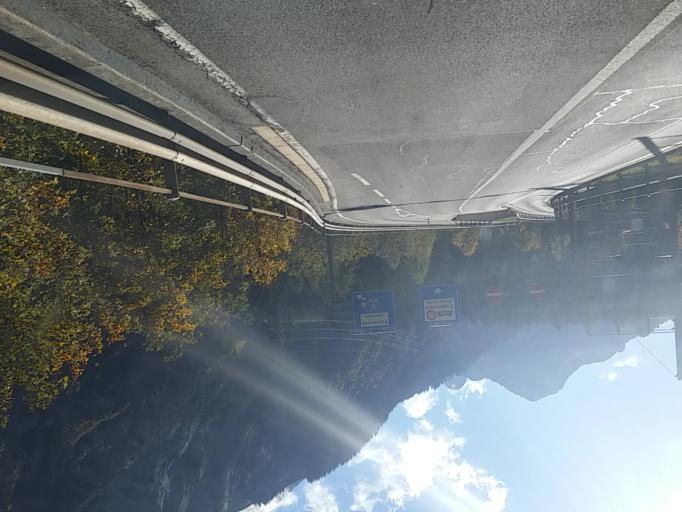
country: CH
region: Bern
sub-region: Frutigen-Niedersimmental District
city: Kandersteg
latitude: 46.5103
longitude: 7.6765
